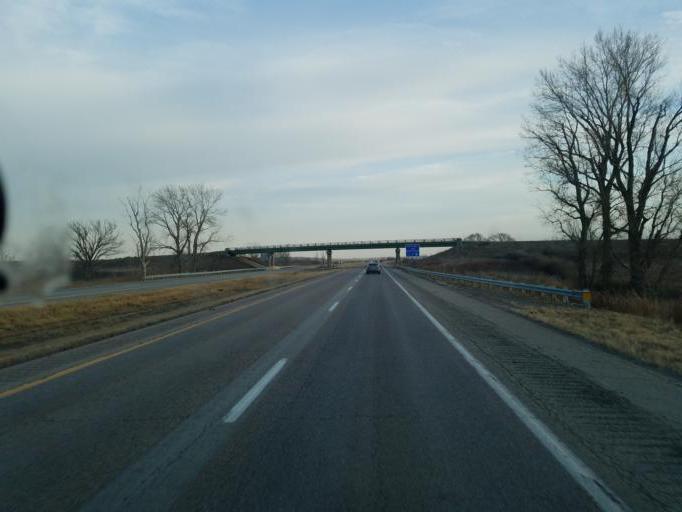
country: US
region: Iowa
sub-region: Harrison County
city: Missouri Valley
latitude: 41.6048
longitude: -95.9681
